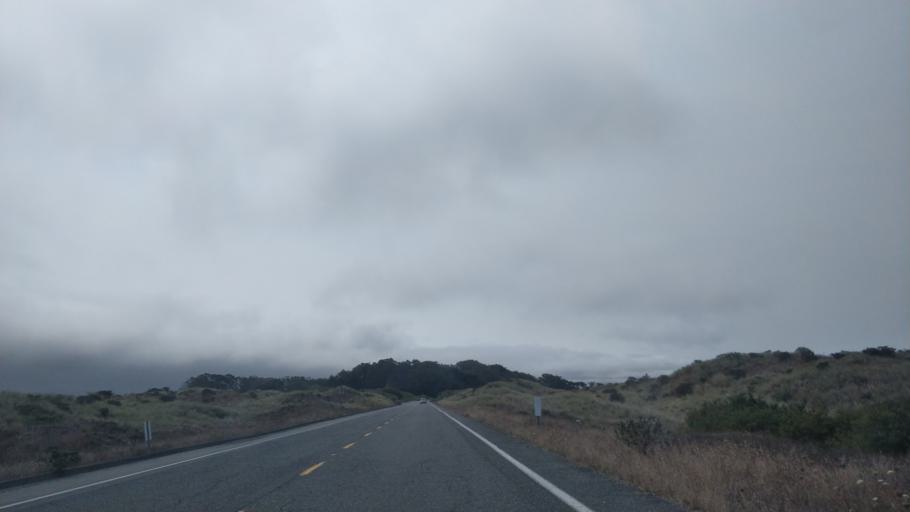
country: US
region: California
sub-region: Humboldt County
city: Bayview
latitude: 40.7856
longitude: -124.2069
